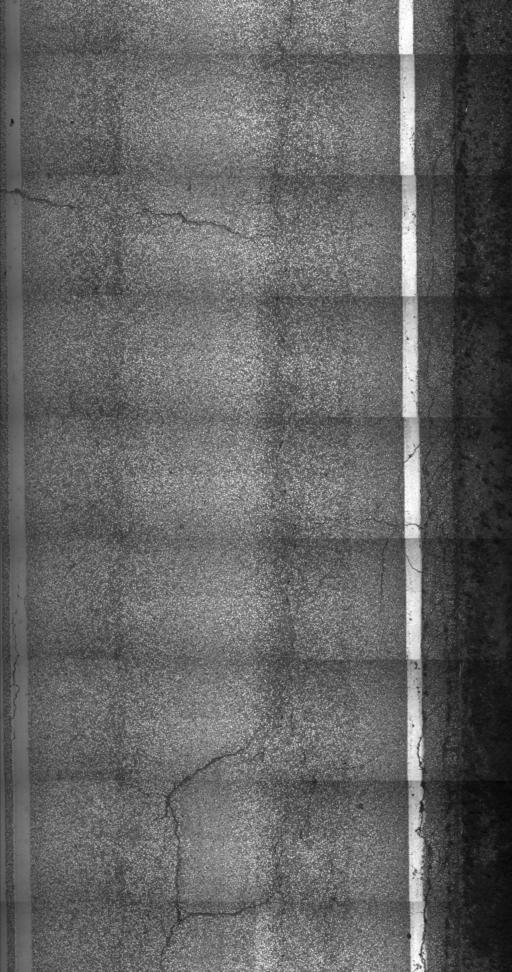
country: US
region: Vermont
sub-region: Washington County
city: Montpelier
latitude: 44.3827
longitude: -72.5527
